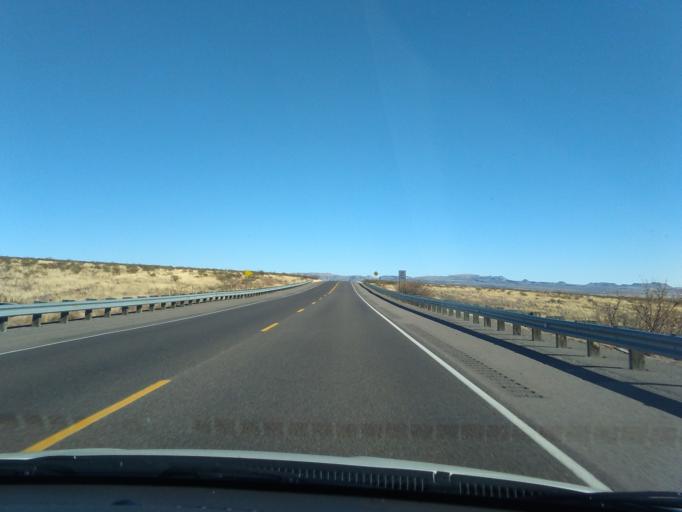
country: US
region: New Mexico
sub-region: Dona Ana County
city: Hatch
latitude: 32.5744
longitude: -107.4144
